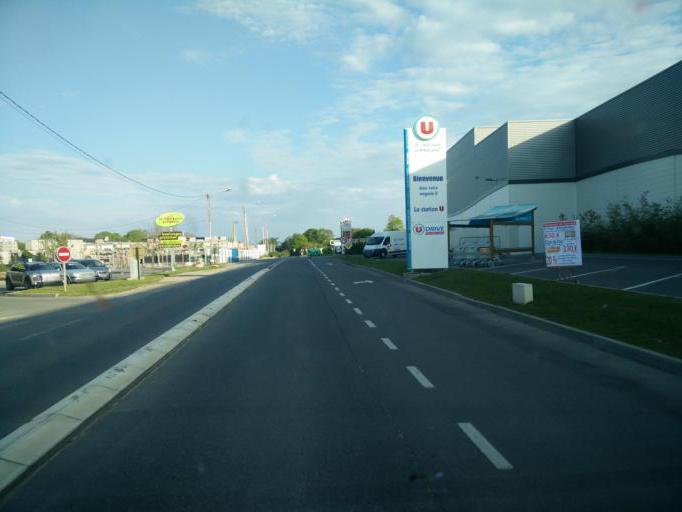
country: FR
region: Brittany
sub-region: Departement des Cotes-d'Armor
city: Erquy
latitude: 48.6225
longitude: -2.4395
